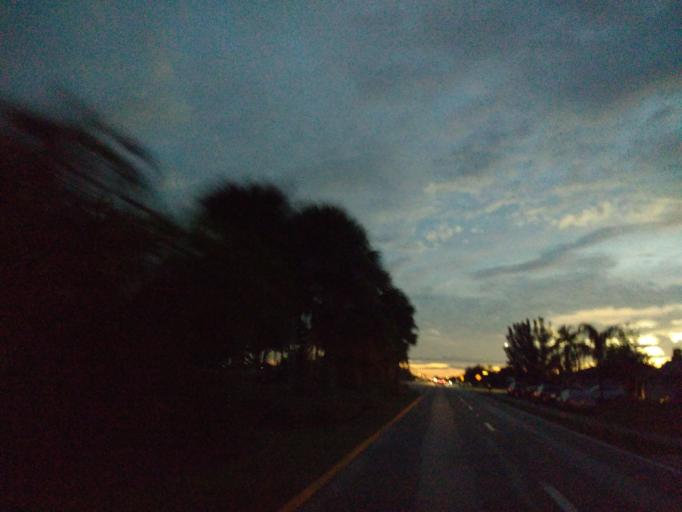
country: US
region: Florida
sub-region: Lee County
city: Cape Coral
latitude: 26.6230
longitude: -81.9826
